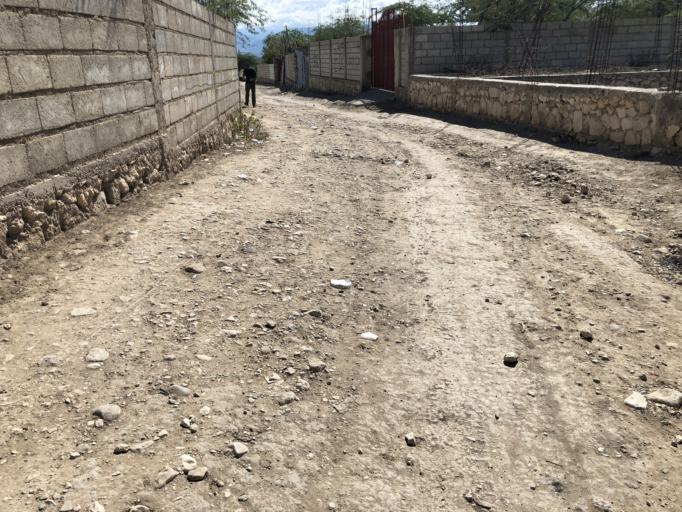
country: HT
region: Ouest
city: Croix des Bouquets
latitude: 18.6568
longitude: -72.2347
